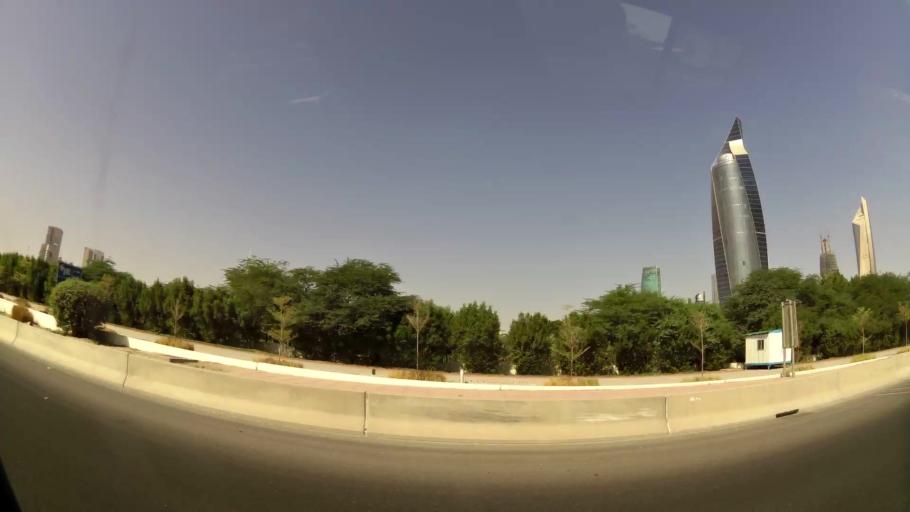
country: KW
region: Al Asimah
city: Ad Dasmah
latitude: 29.3663
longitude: 47.9934
